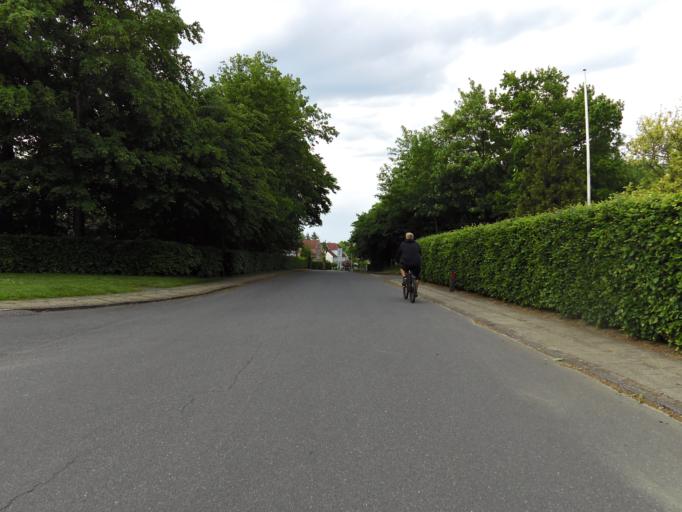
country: DK
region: South Denmark
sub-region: Haderslev Kommune
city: Gram
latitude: 55.2858
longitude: 9.0461
